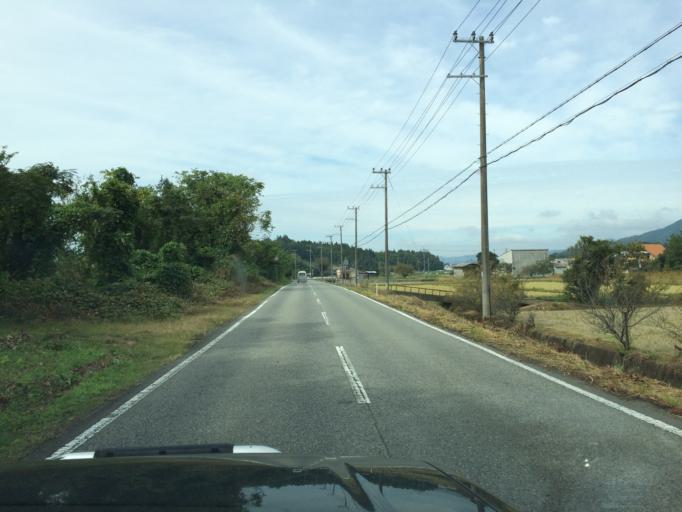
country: JP
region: Hyogo
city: Sasayama
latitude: 35.0736
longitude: 135.2372
